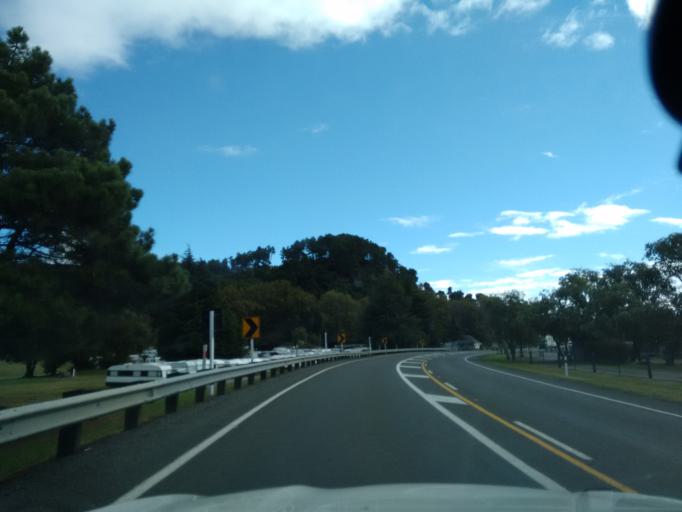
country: NZ
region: Waikato
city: Turangi
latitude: -38.8873
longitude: 175.9602
